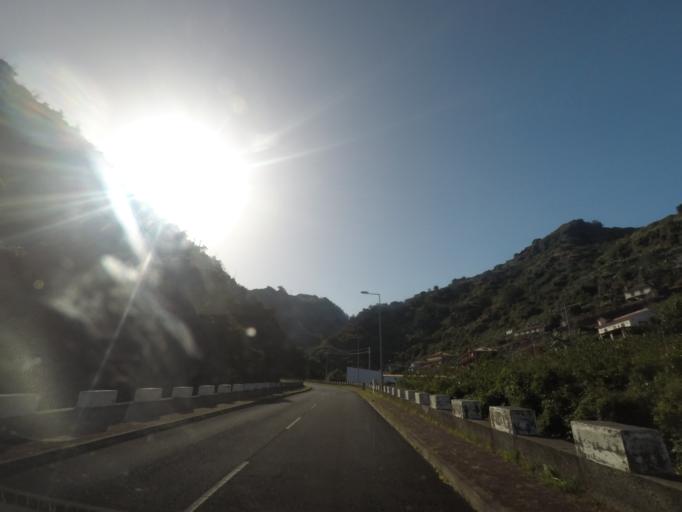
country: PT
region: Madeira
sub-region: Santa Cruz
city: Santa Cruz
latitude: 32.6915
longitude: -16.7997
